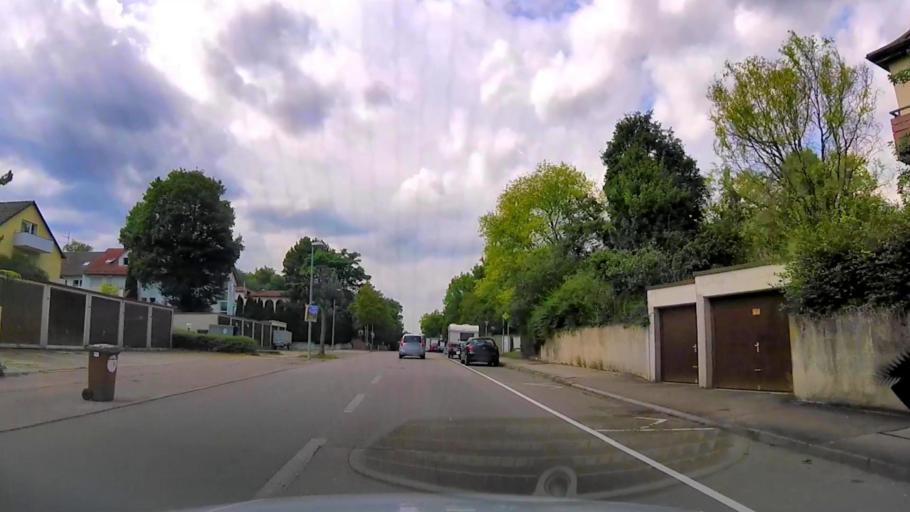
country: DE
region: Baden-Wuerttemberg
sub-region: Regierungsbezirk Stuttgart
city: Korntal
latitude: 48.8140
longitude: 9.1331
